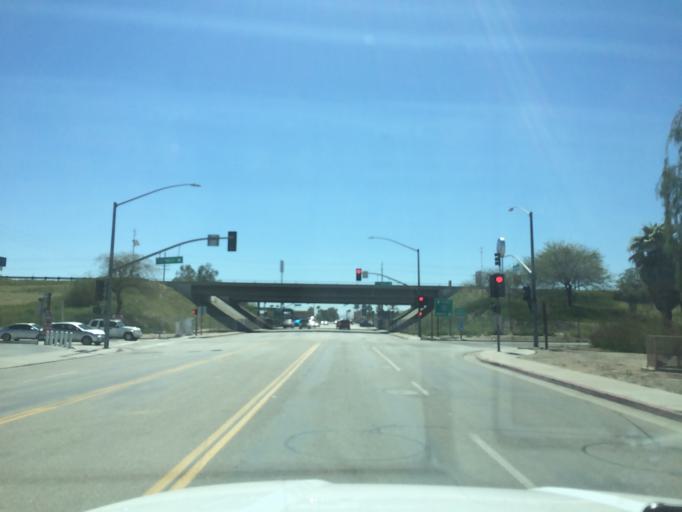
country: US
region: California
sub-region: Riverside County
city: Blythe
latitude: 33.6081
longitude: -114.6055
